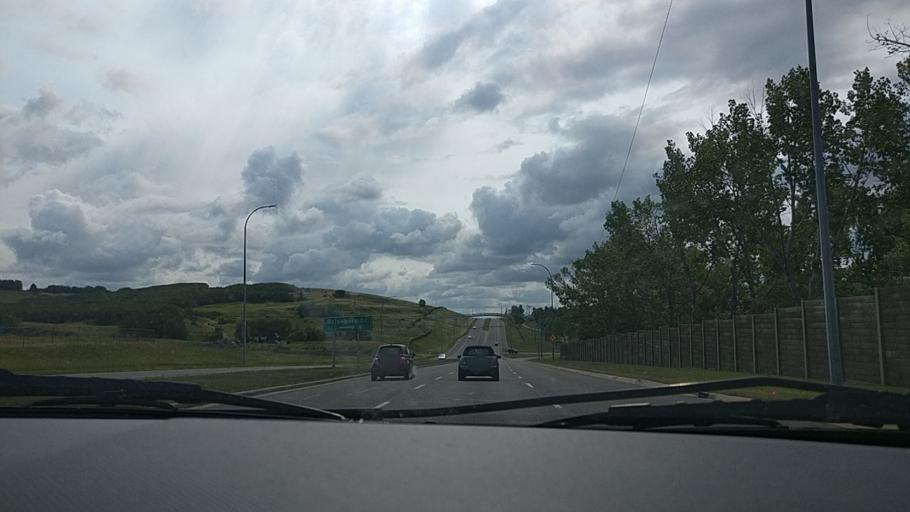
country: CA
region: Alberta
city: Calgary
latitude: 51.1049
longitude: -114.1306
